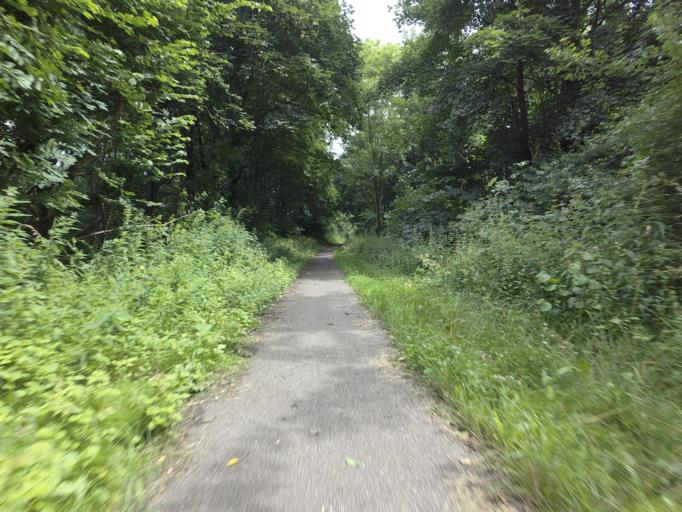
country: DK
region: Central Jutland
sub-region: Randers Kommune
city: Langa
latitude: 56.3313
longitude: 9.8949
